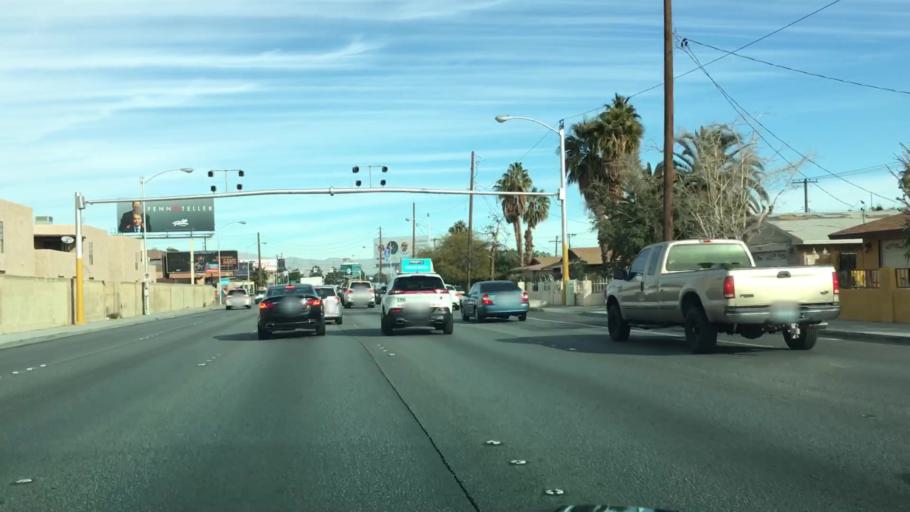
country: US
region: Nevada
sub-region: Clark County
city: Paradise
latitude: 36.0972
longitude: -115.1457
